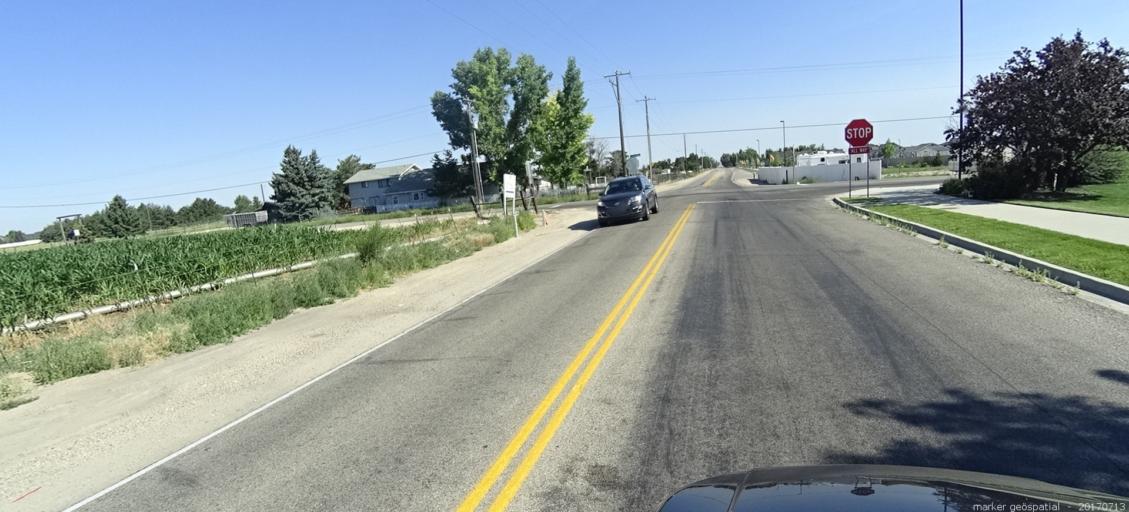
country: US
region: Idaho
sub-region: Ada County
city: Kuna
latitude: 43.5171
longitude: -116.4138
